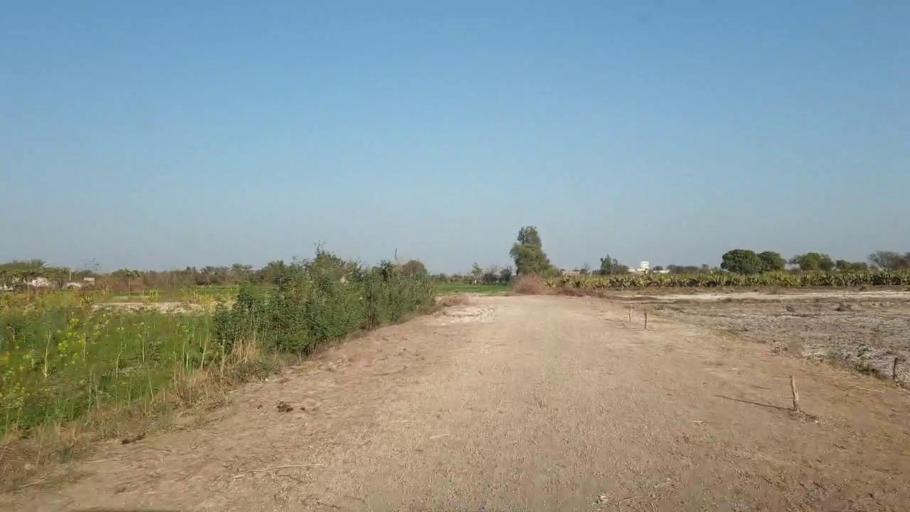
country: PK
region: Sindh
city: Tando Allahyar
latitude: 25.3764
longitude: 68.6983
